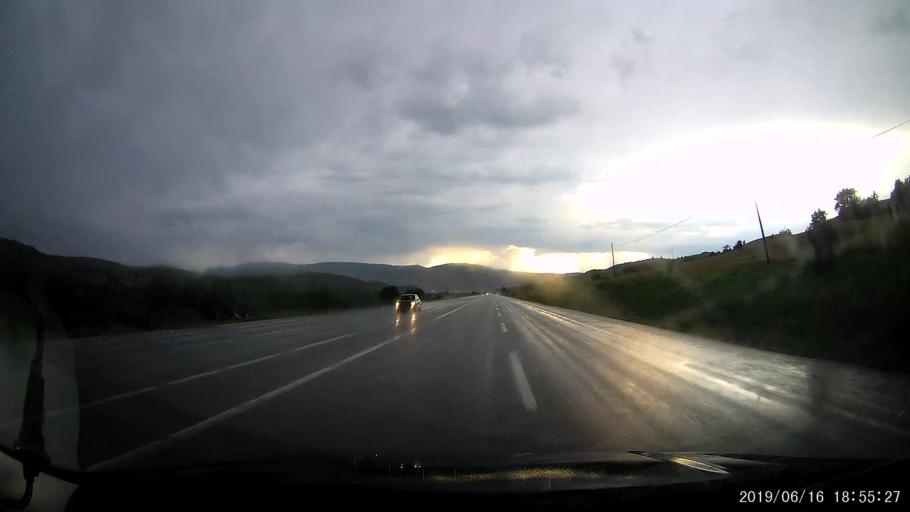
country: TR
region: Erzincan
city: Refahiye
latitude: 39.9002
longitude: 38.8275
